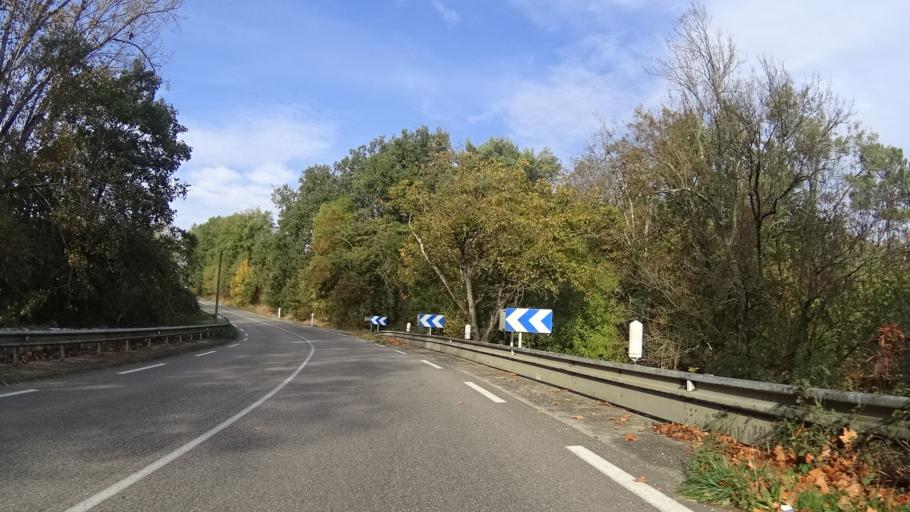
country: FR
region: Aquitaine
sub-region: Departement du Lot-et-Garonne
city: Boe
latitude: 44.1627
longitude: 0.6178
